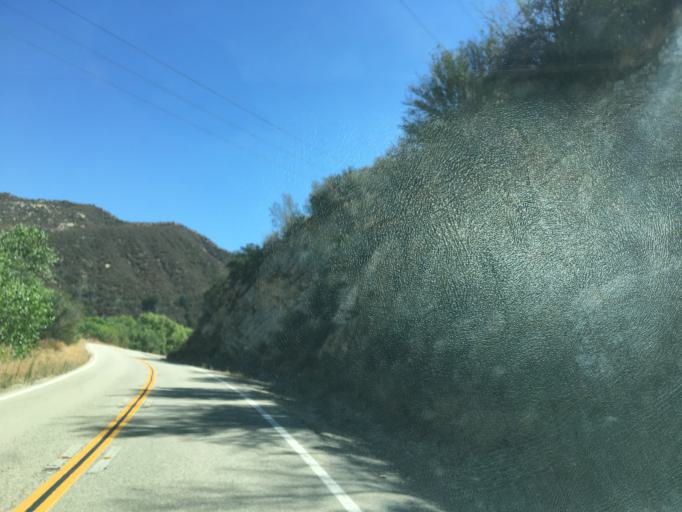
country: US
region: California
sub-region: Los Angeles County
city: Castaic
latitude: 34.6040
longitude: -118.5597
